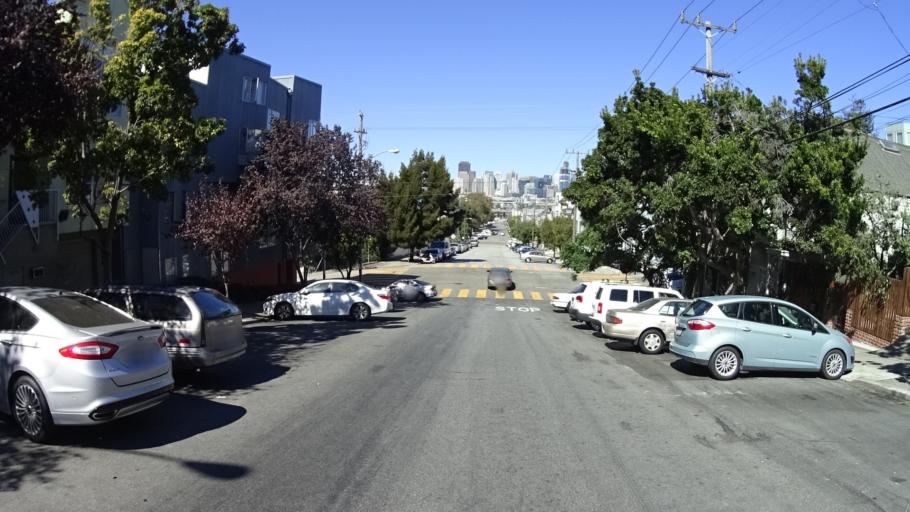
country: US
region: California
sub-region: San Francisco County
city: San Francisco
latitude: 37.7620
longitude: -122.3984
